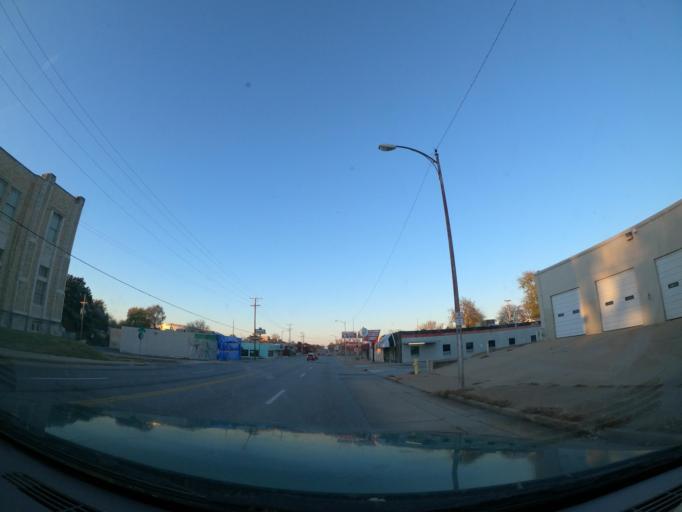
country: US
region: Oklahoma
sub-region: Tulsa County
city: Tulsa
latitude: 36.1458
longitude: -95.9403
